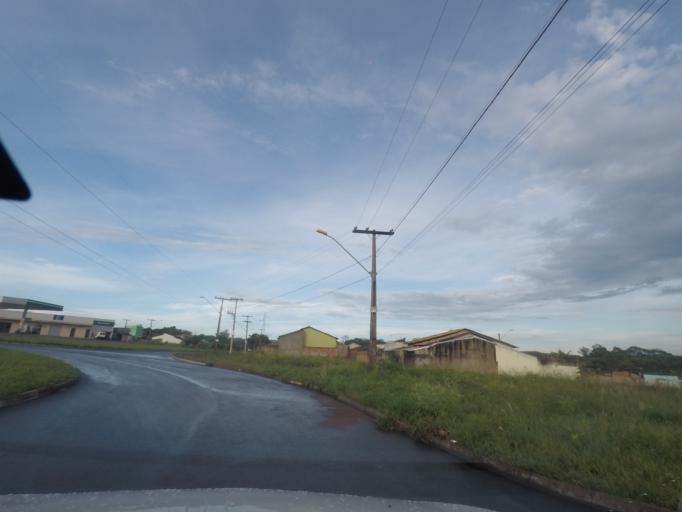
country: BR
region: Goias
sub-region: Goiania
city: Goiania
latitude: -16.7387
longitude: -49.3699
